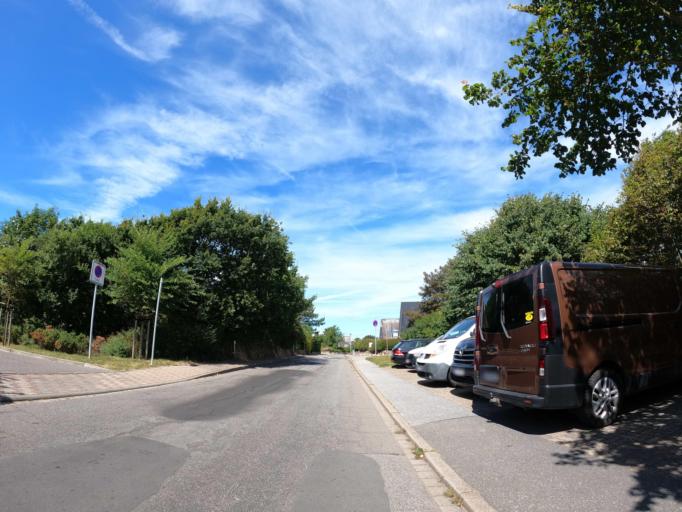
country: DE
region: Schleswig-Holstein
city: Westerland
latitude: 54.9118
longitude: 8.3171
